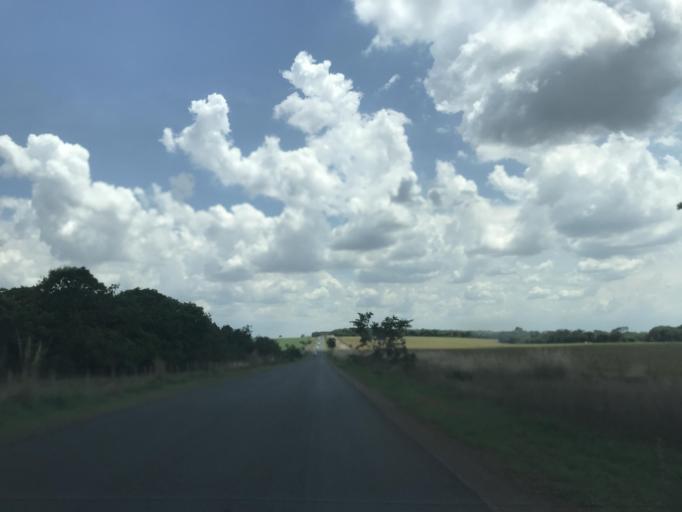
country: BR
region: Goias
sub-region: Piracanjuba
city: Piracanjuba
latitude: -17.3508
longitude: -48.7942
